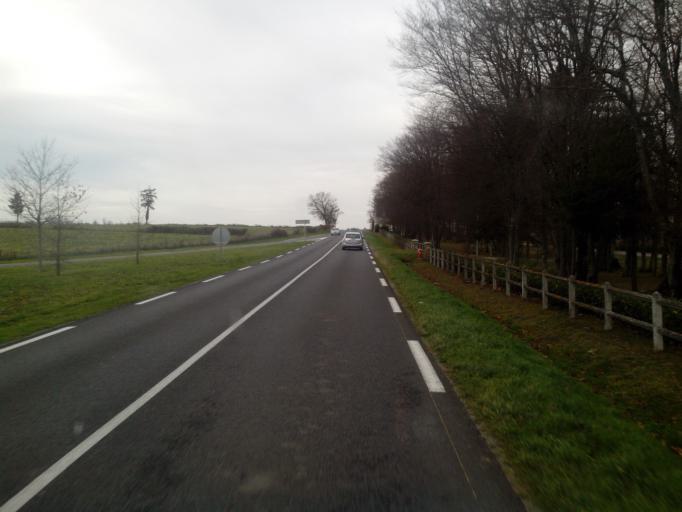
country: FR
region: Limousin
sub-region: Departement de la Haute-Vienne
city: Magnac-Laval
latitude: 46.2092
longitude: 1.1843
